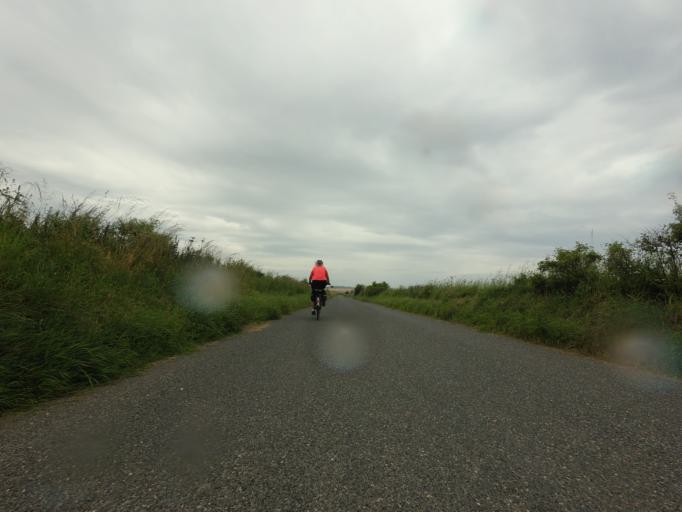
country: GB
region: Scotland
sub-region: Aberdeenshire
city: Whitehills
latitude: 57.6729
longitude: -2.6357
